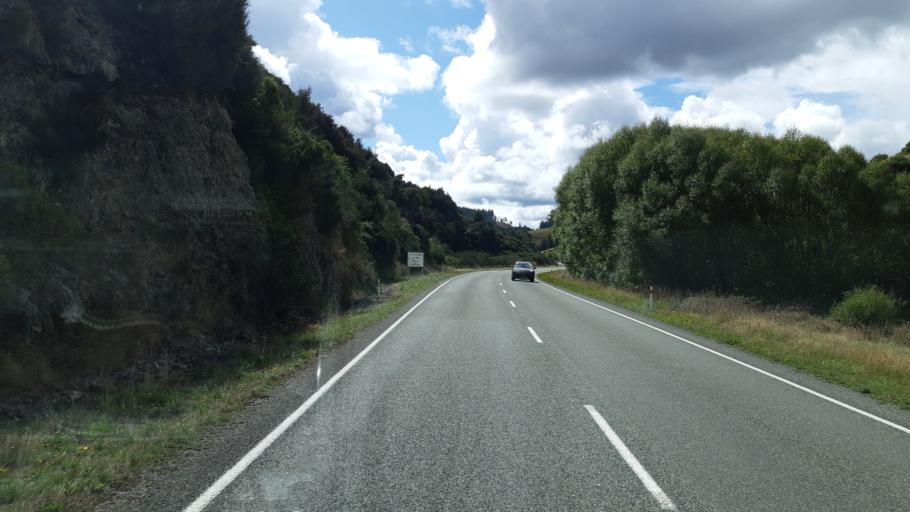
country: NZ
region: Tasman
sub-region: Tasman District
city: Wakefield
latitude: -41.6466
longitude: 172.6546
